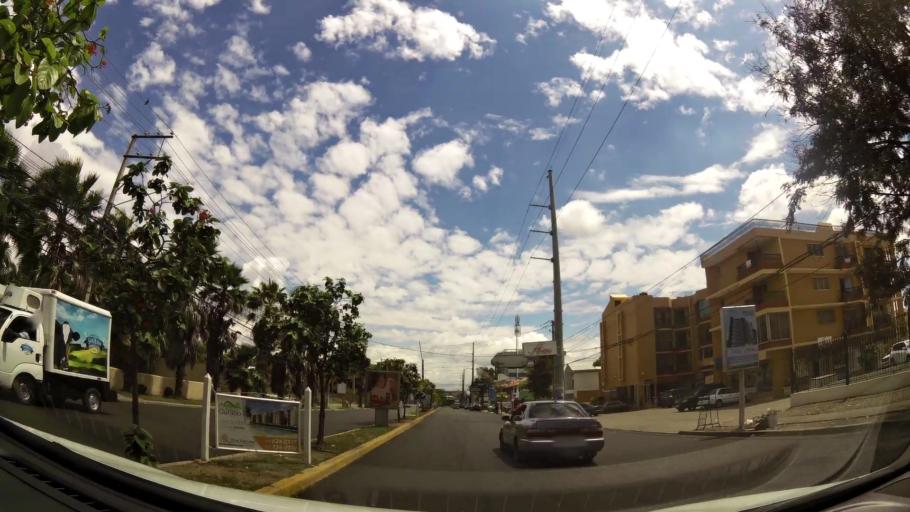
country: DO
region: Santiago
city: Santiago de los Caballeros
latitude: 19.4585
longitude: -70.6743
